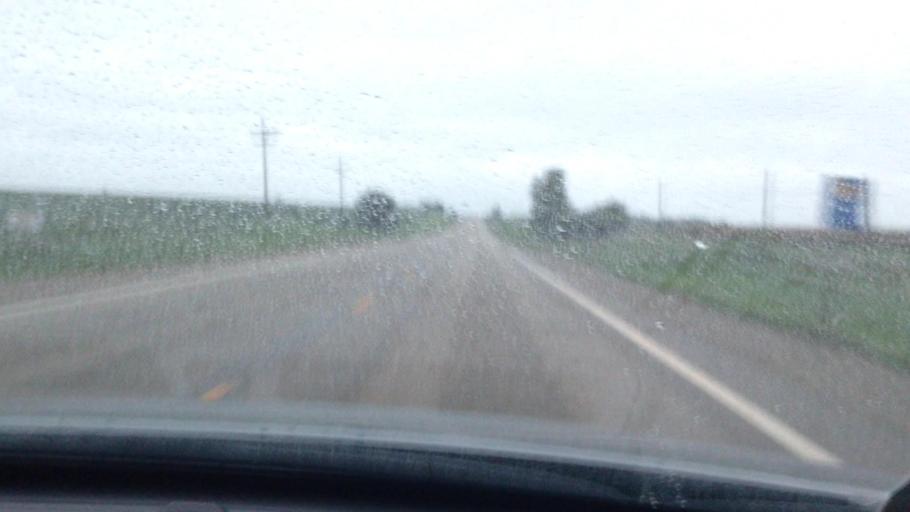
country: US
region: Kansas
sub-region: Brown County
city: Hiawatha
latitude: 39.8131
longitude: -95.5273
